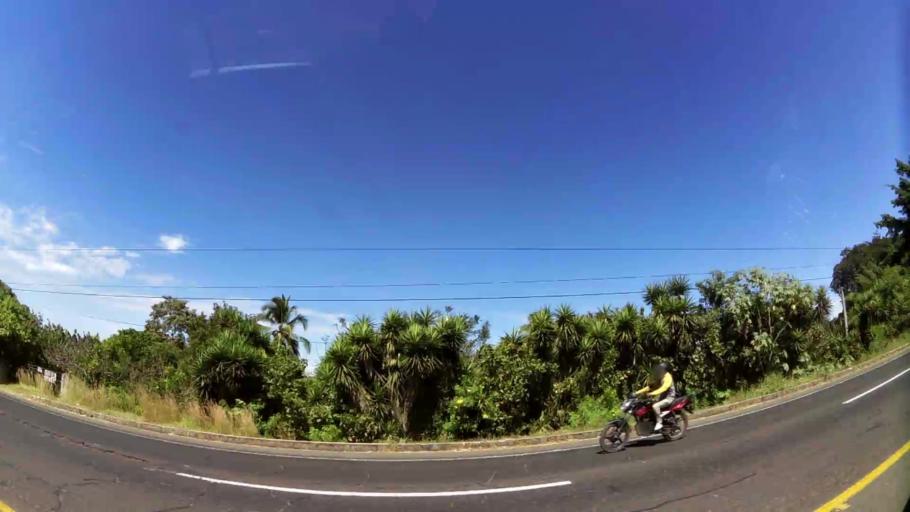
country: SV
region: Ahuachapan
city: Atiquizaya
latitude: 13.9723
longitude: -89.7209
